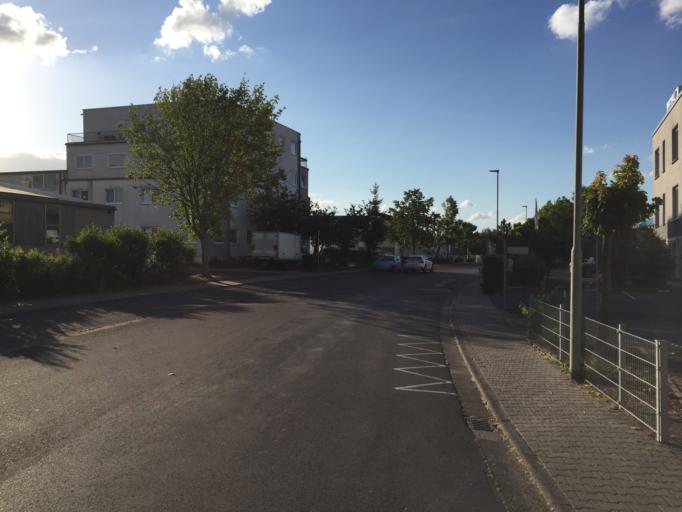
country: DE
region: Hesse
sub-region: Regierungsbezirk Darmstadt
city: Karben
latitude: 50.2239
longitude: 8.7647
